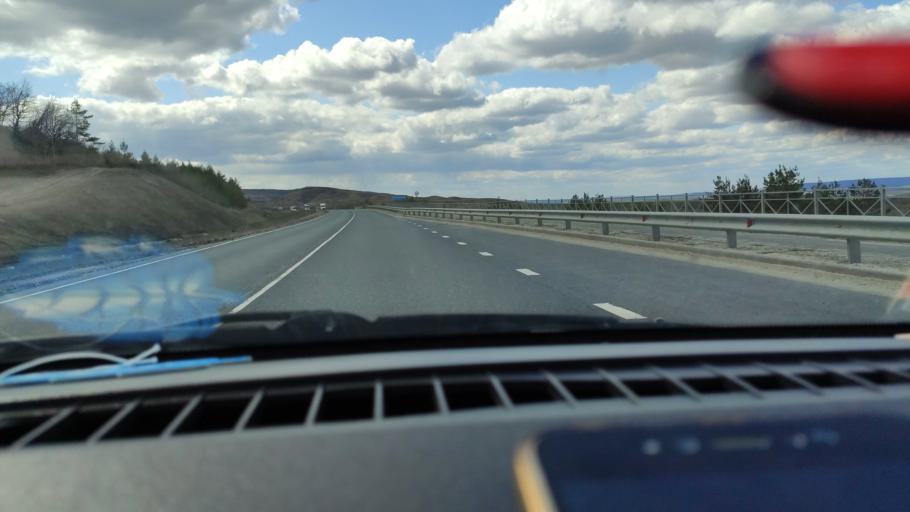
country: RU
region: Saratov
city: Alekseyevka
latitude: 52.3839
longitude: 47.9736
